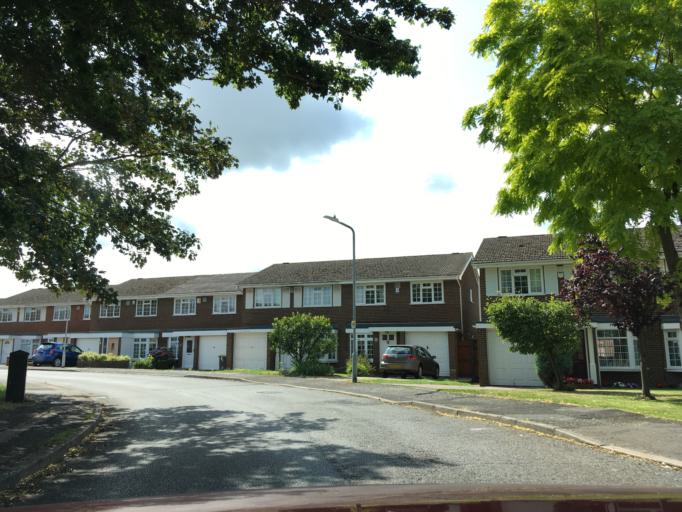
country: GB
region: England
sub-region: Kent
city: Larkfield
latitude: 51.2939
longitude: 0.4518
